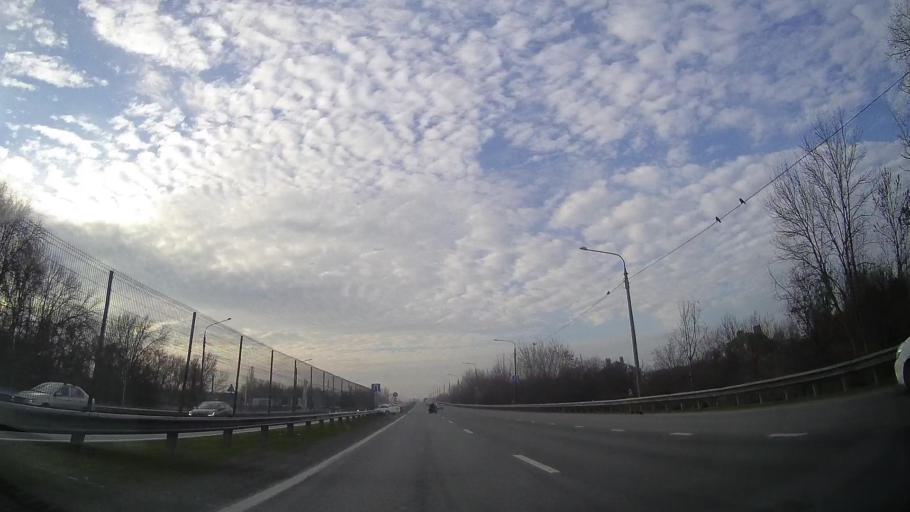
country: RU
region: Rostov
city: Bataysk
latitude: 47.1258
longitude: 39.7737
